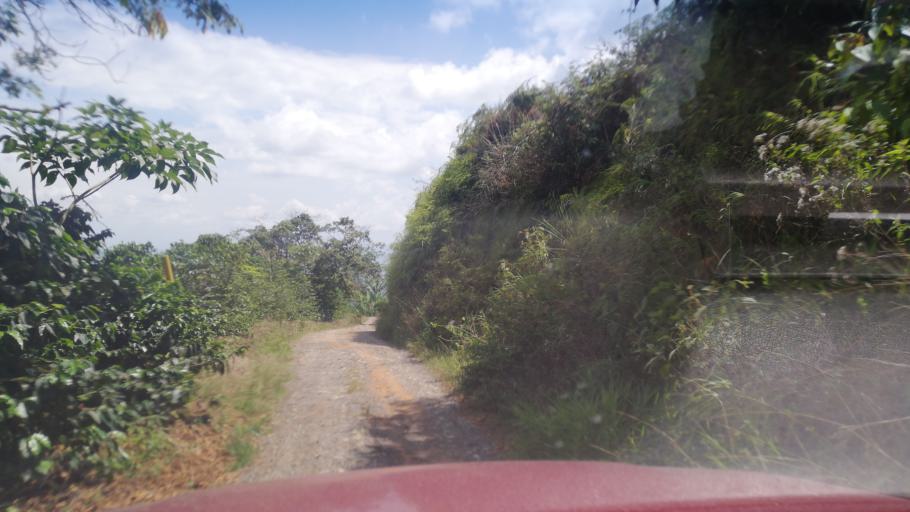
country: CO
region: Risaralda
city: Balboa
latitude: 4.9313
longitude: -75.9654
